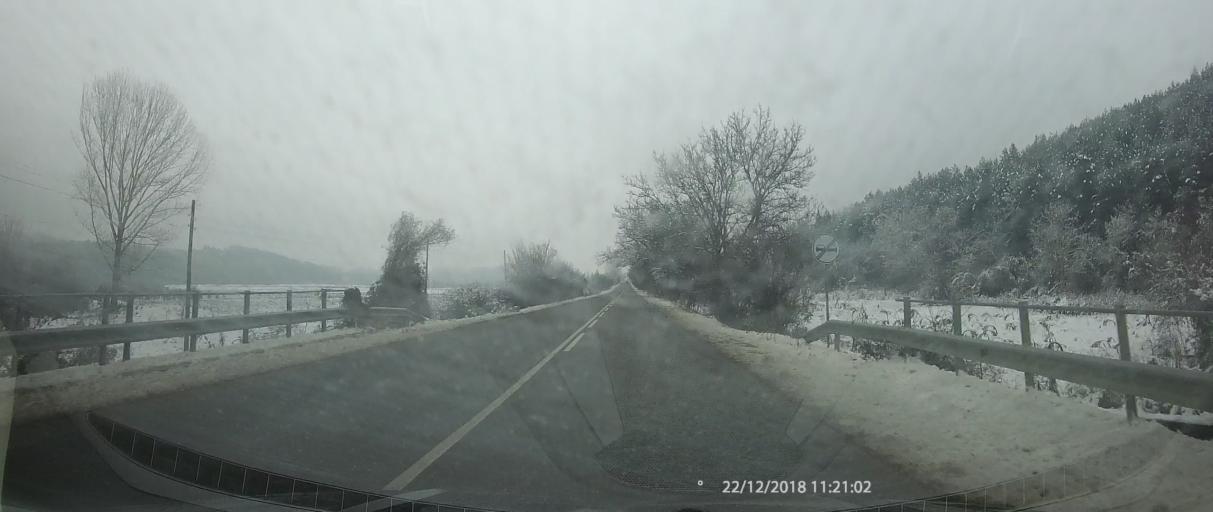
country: BG
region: Kyustendil
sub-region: Obshtina Kyustendil
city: Kyustendil
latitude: 42.2605
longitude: 22.8321
